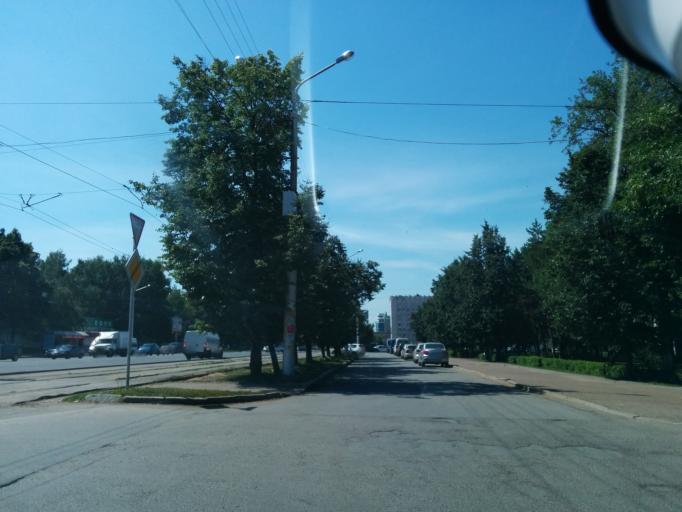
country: RU
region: Bashkortostan
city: Ufa
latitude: 54.7525
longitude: 55.9884
